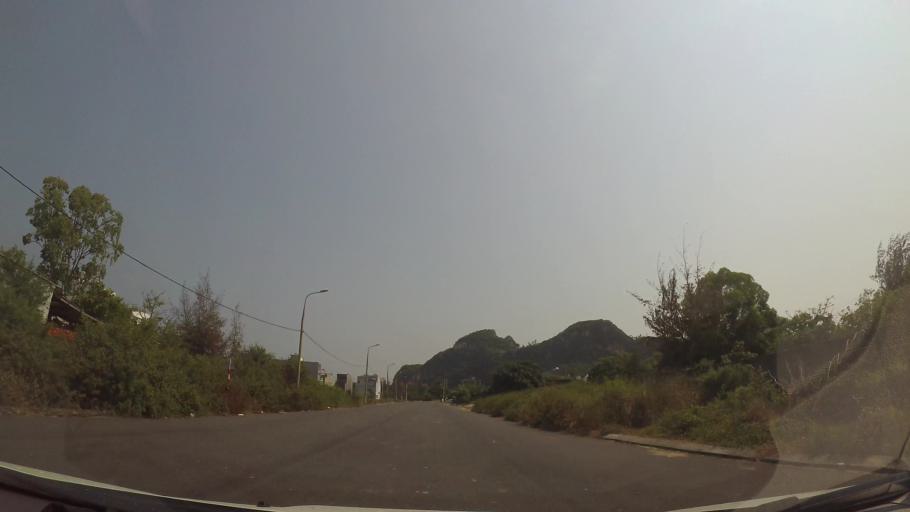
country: VN
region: Da Nang
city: Ngu Hanh Son
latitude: 16.0095
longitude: 108.2618
